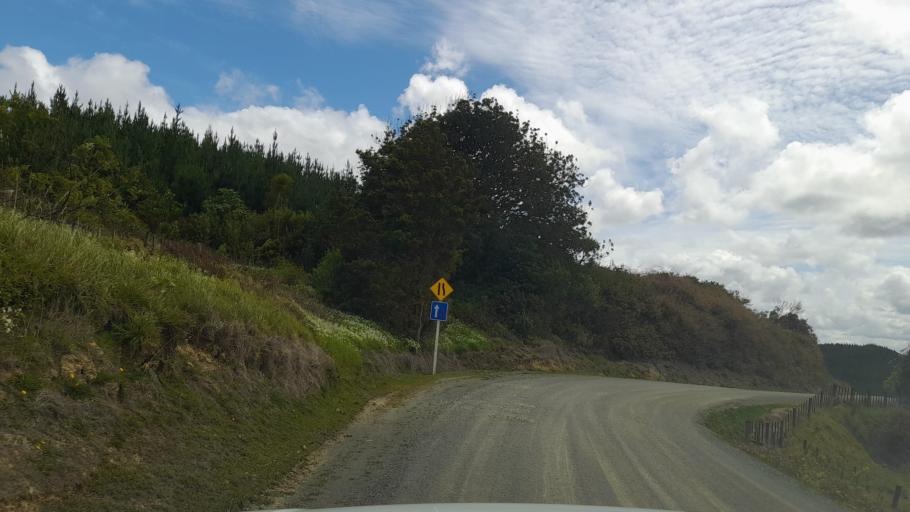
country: NZ
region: Auckland
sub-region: Auckland
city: Wellsford
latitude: -36.1762
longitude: 174.3490
